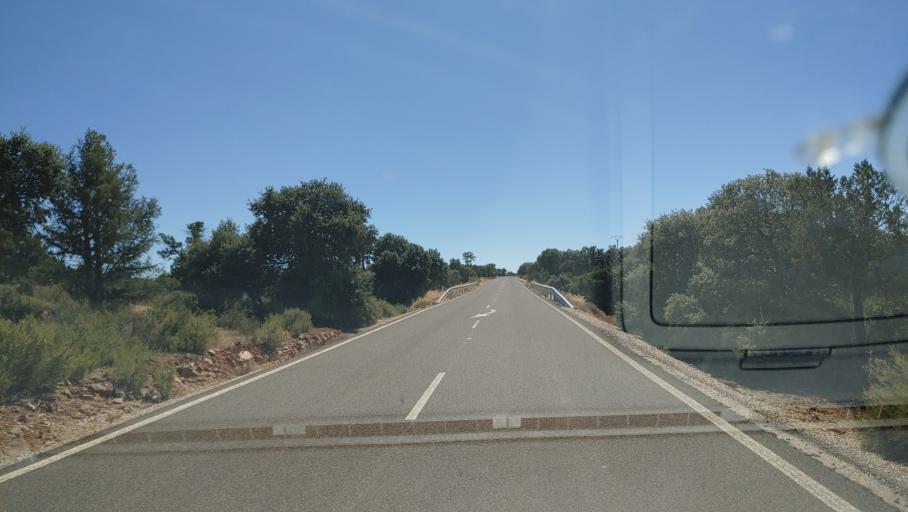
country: ES
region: Castille-La Mancha
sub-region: Provincia de Ciudad Real
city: Villahermosa
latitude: 38.8482
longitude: -2.8077
